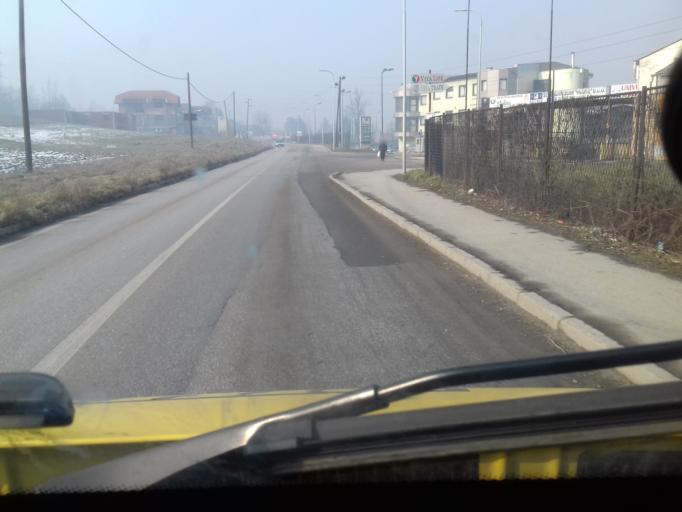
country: BA
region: Federation of Bosnia and Herzegovina
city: Visoko
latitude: 43.9995
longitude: 18.1630
